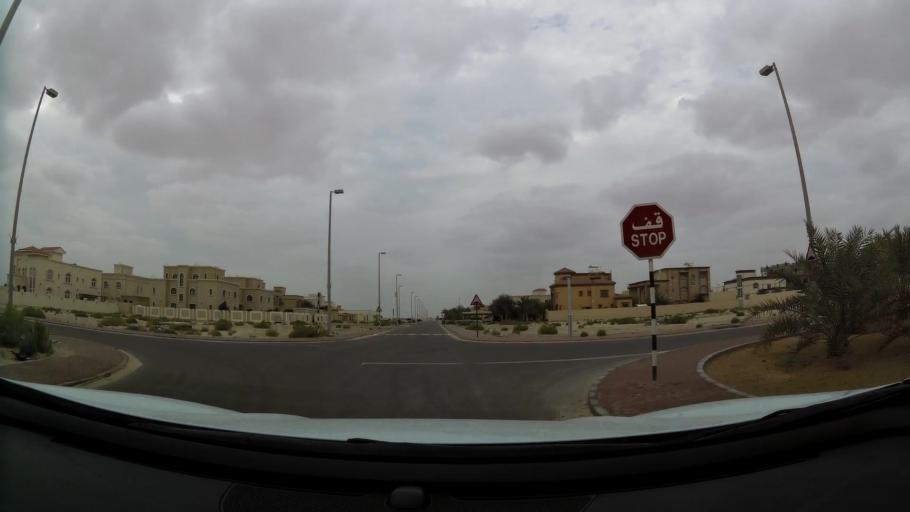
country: AE
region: Abu Dhabi
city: Abu Dhabi
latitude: 24.3735
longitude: 54.6348
